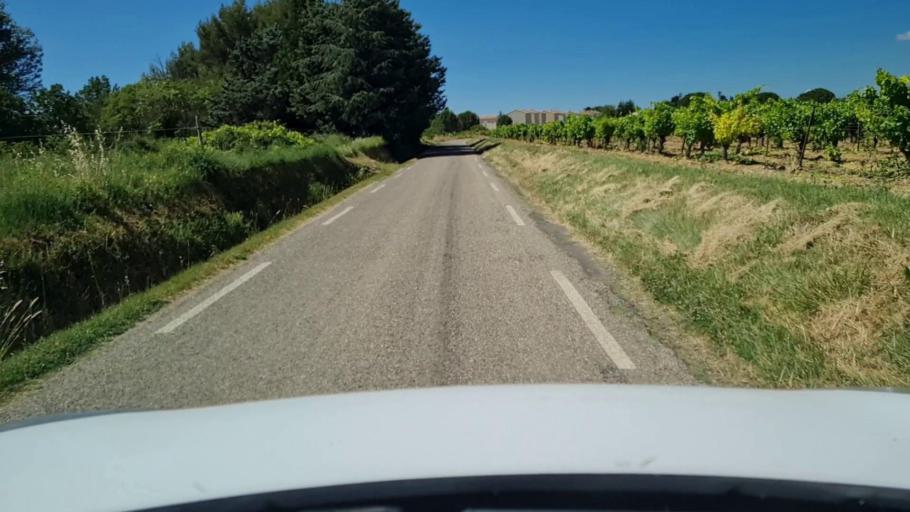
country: FR
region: Languedoc-Roussillon
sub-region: Departement du Gard
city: Saint-Mamert-du-Gard
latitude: 43.8579
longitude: 4.1627
